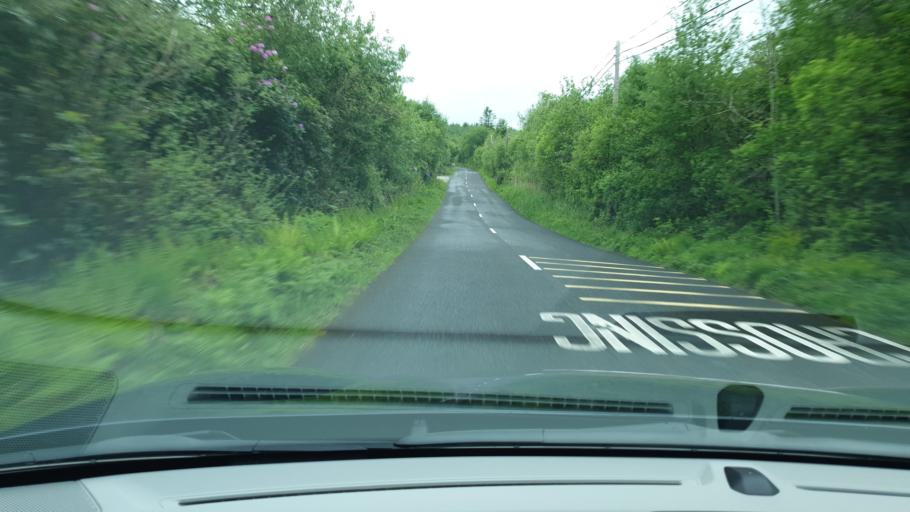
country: IE
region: Connaught
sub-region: County Galway
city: Clifden
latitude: 53.4576
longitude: -9.8591
